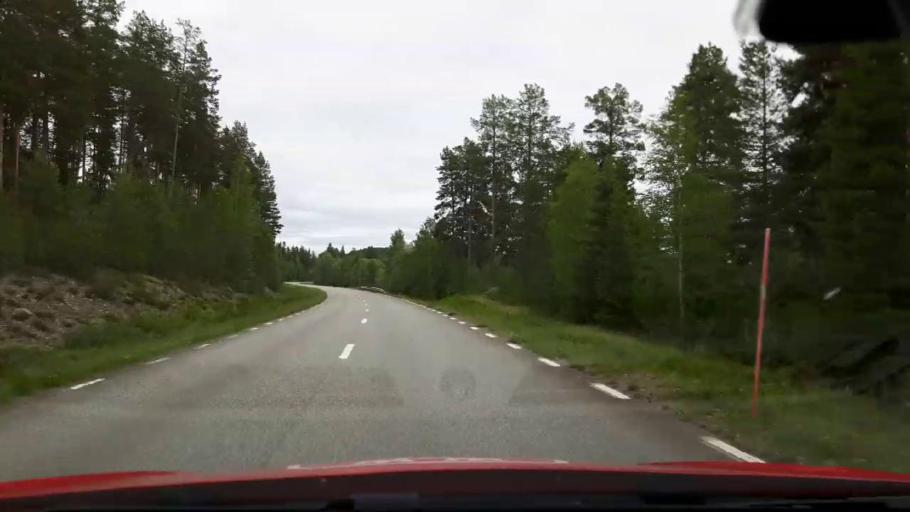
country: SE
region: Jaemtland
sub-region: Stroemsunds Kommun
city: Stroemsund
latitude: 63.3693
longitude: 15.7049
